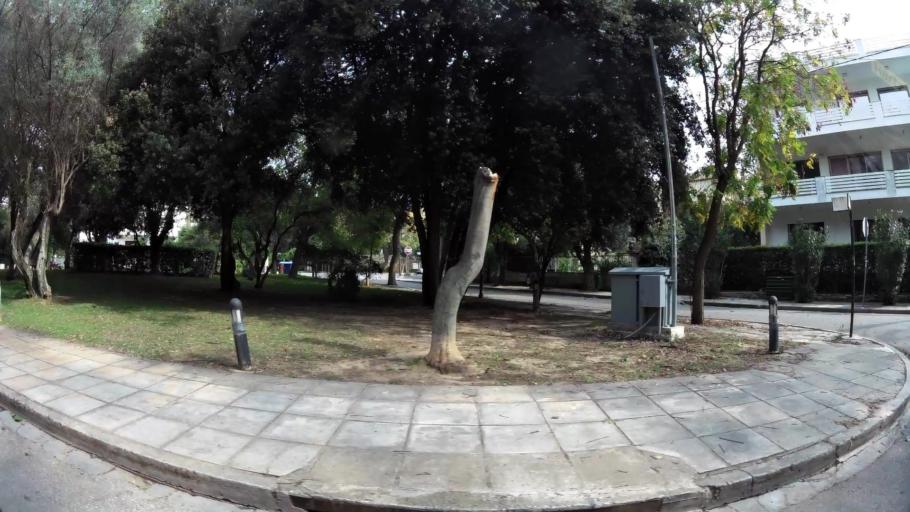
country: GR
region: Attica
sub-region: Nomarchia Athinas
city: Filothei
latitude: 38.0251
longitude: 23.7805
